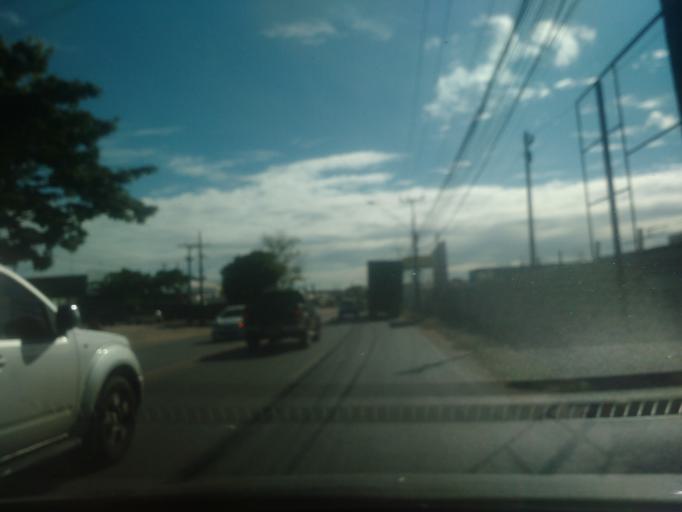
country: BR
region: Alagoas
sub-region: Satuba
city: Satuba
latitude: -9.5599
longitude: -35.7651
